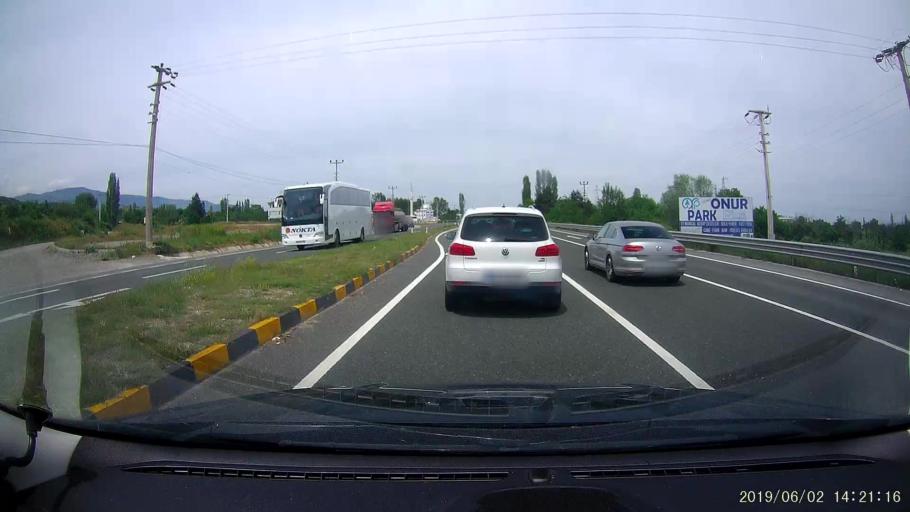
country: TR
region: Kastamonu
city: Tosya
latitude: 40.9774
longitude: 34.0010
